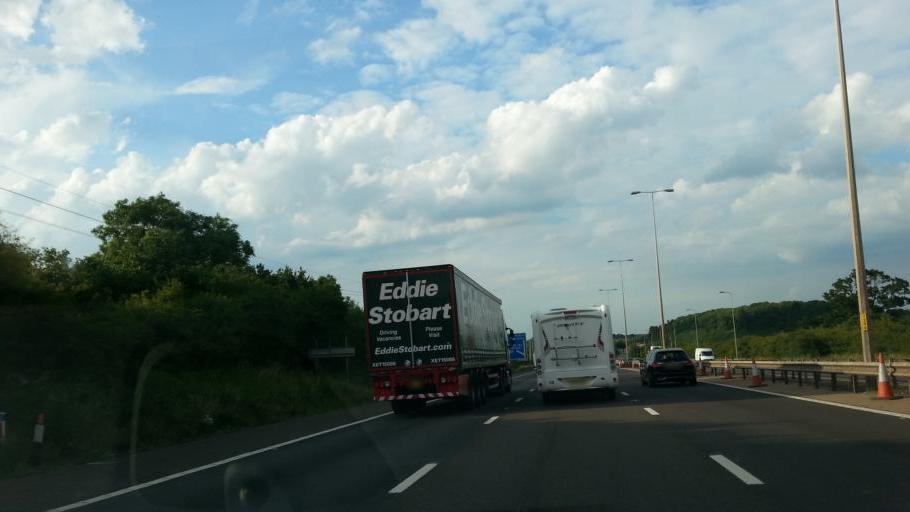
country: GB
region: England
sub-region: Worcestershire
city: Fernhill Heath
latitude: 52.2050
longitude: -2.1618
